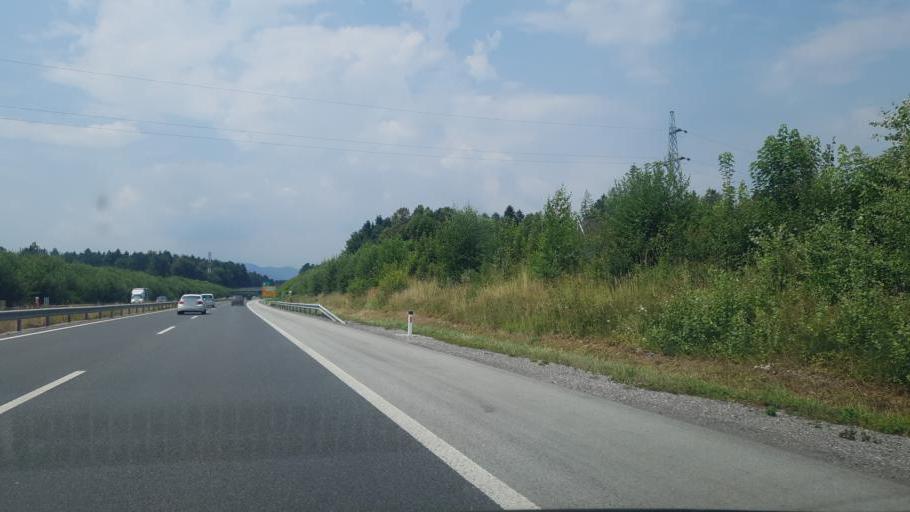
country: SI
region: Kranj
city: Kokrica
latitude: 46.2627
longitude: 14.3529
